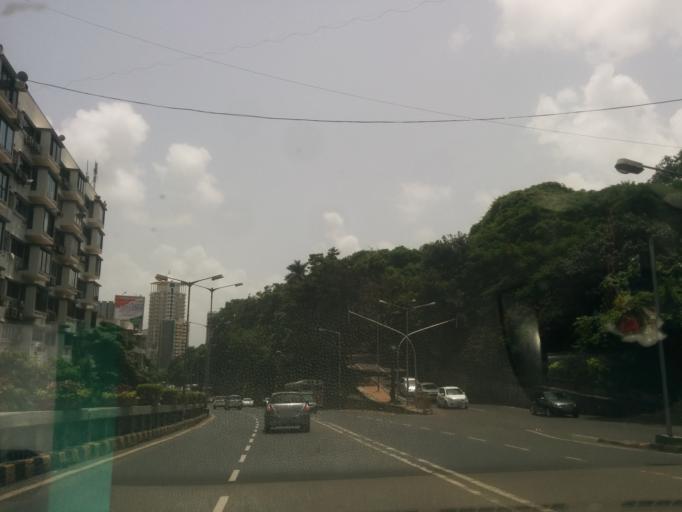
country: IN
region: Maharashtra
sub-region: Mumbai Suburban
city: Mumbai
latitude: 18.9634
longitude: 72.8076
